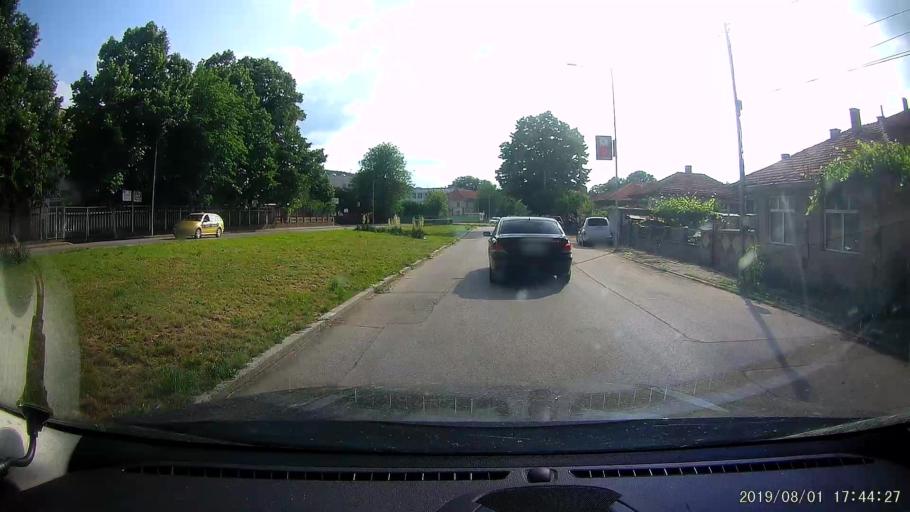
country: BG
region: Silistra
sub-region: Obshtina Silistra
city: Silistra
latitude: 44.1098
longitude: 27.2686
